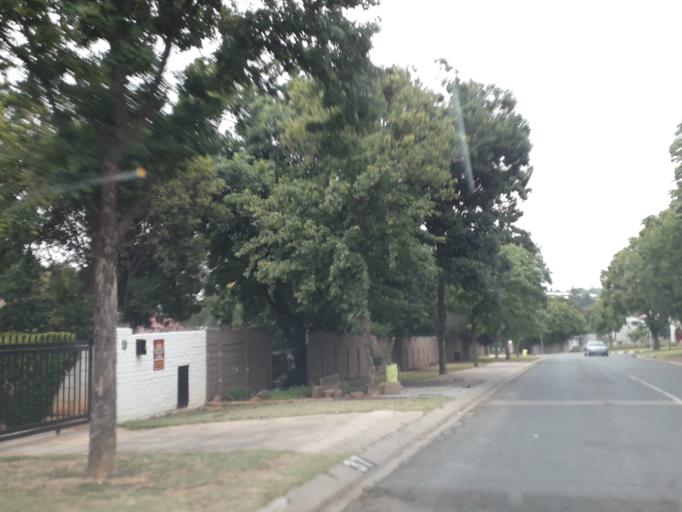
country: ZA
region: Gauteng
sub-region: City of Johannesburg Metropolitan Municipality
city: Roodepoort
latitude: -26.1103
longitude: 27.9442
